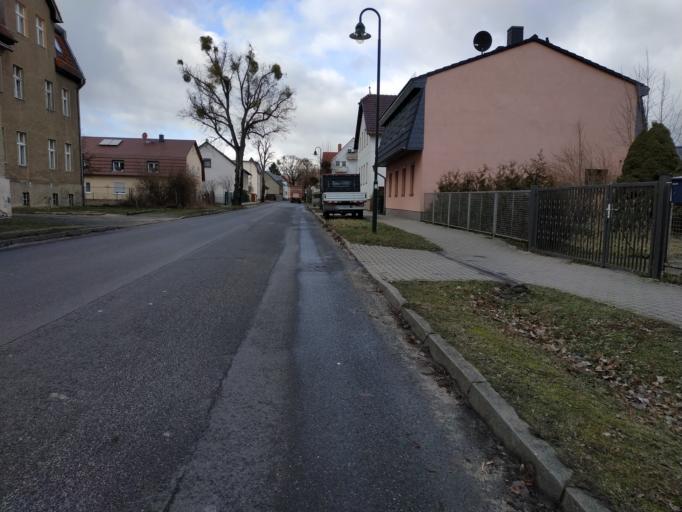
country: DE
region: Brandenburg
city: Petershagen
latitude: 52.5353
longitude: 13.8169
